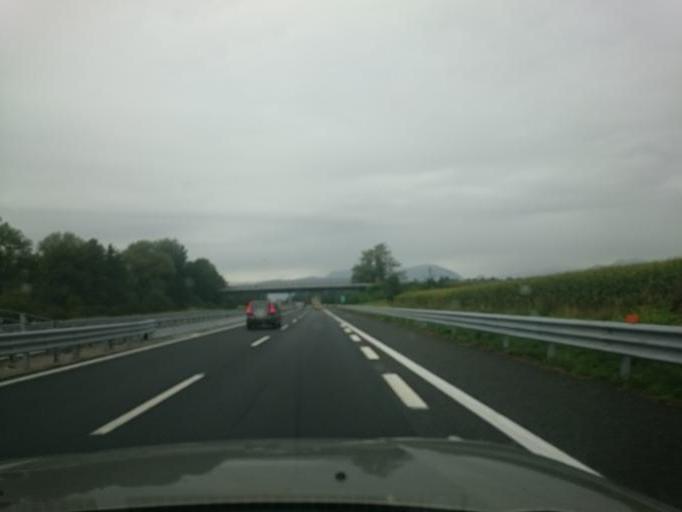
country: IT
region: Friuli Venezia Giulia
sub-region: Provincia di Udine
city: Collofedo di Monte Albano
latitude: 46.1778
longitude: 13.1381
